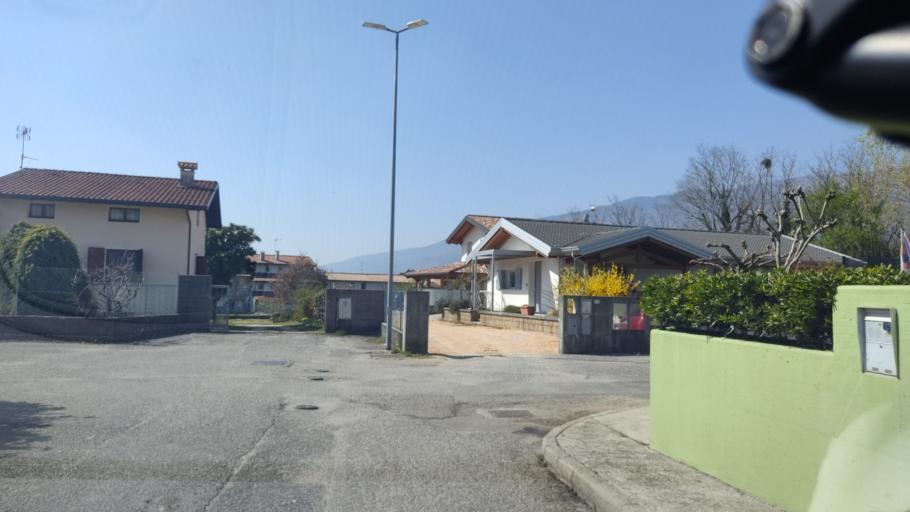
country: IT
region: Friuli Venezia Giulia
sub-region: Provincia di Pordenone
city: Budoia
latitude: 46.0341
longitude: 12.5358
